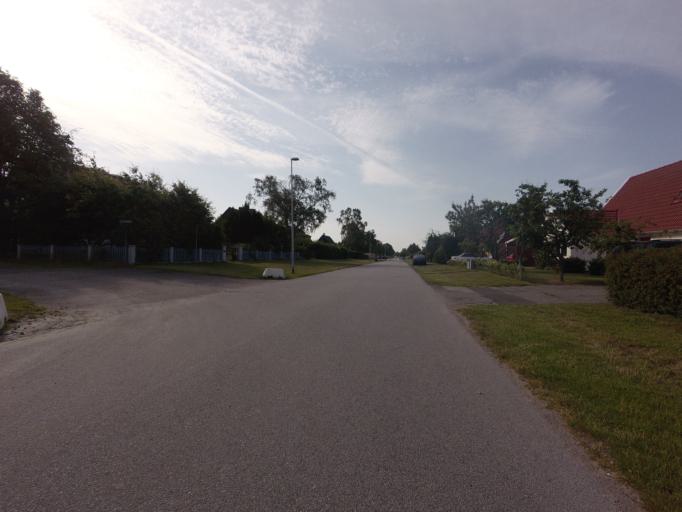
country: SE
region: Skane
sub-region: Malmo
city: Tygelsjo
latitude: 55.4948
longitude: 13.0108
